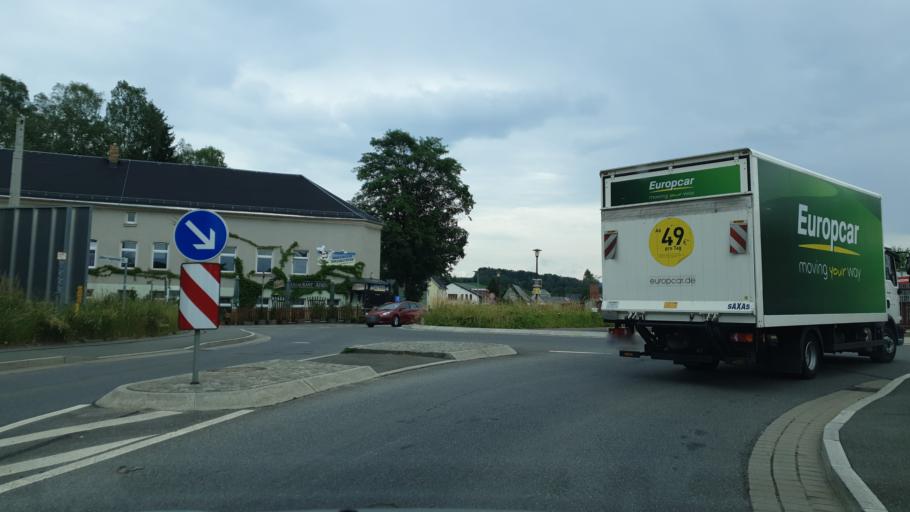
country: DE
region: Saxony
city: Rodewisch
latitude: 50.5416
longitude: 12.3951
